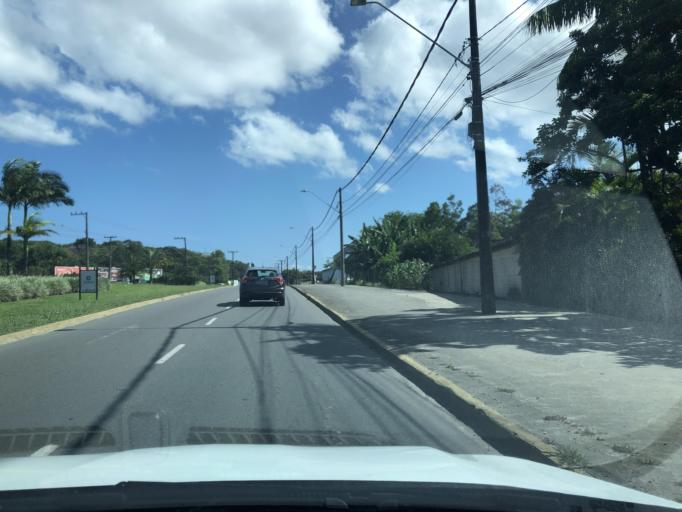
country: BR
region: Santa Catarina
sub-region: Joinville
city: Joinville
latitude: -26.2556
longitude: -48.8520
